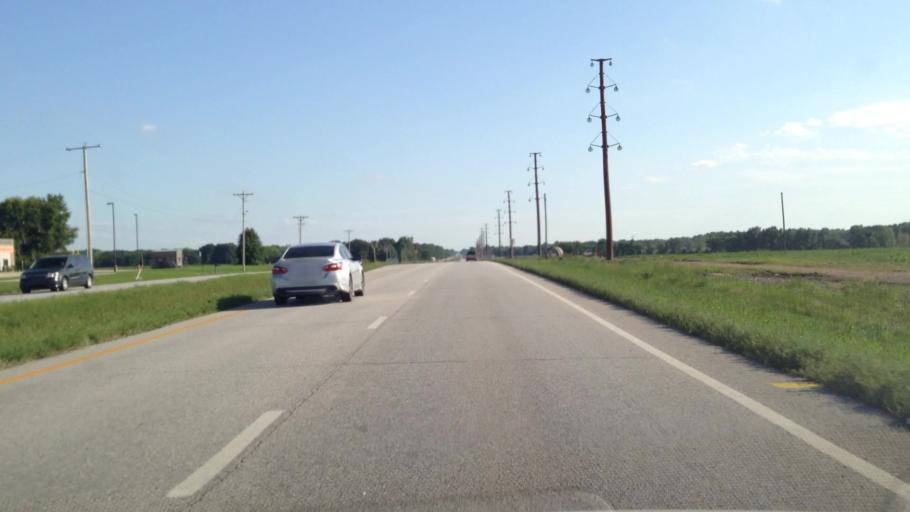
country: US
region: Kansas
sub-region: Crawford County
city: Frontenac
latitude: 37.4895
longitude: -94.7053
